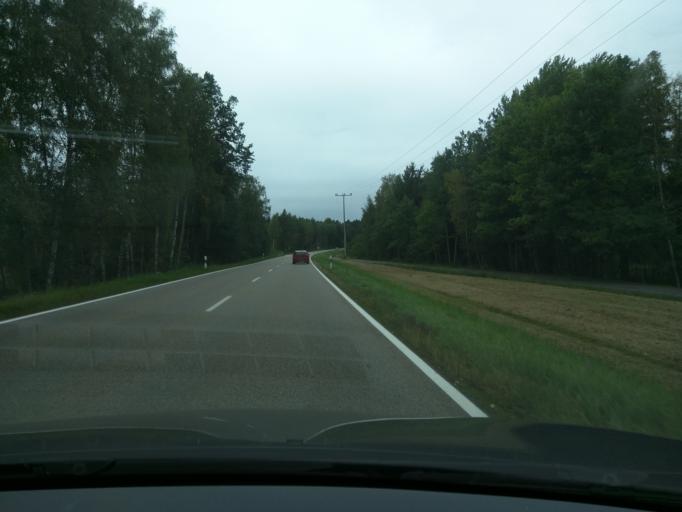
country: DE
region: Bavaria
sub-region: Upper Palatinate
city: Steinberg
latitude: 49.2753
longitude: 12.1531
